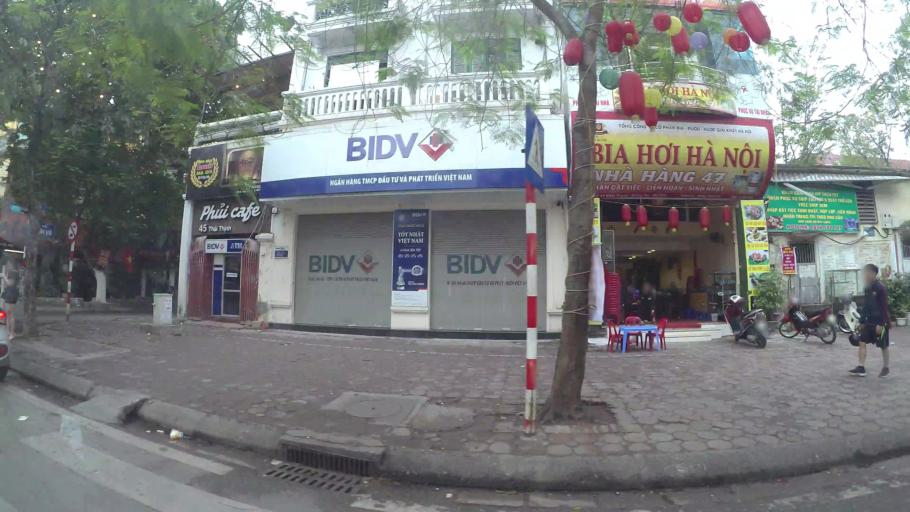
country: VN
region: Ha Noi
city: Dong Da
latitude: 21.0084
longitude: 105.8202
